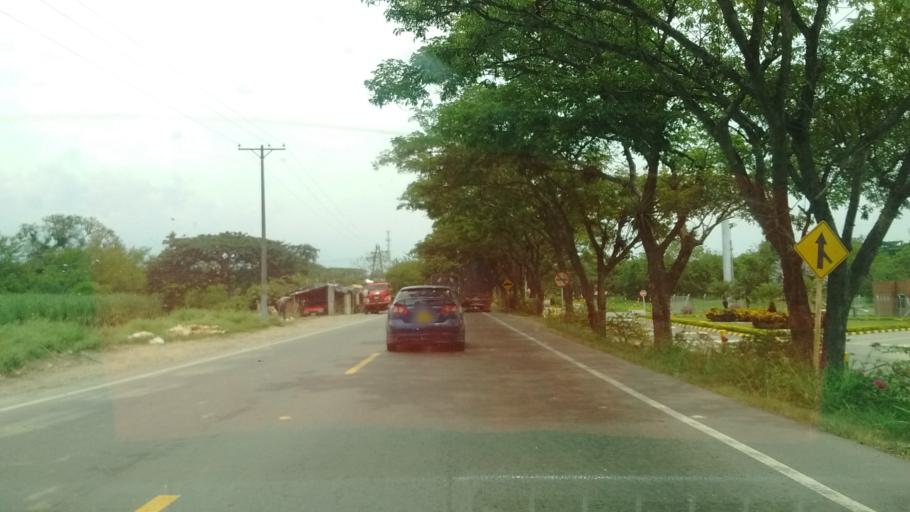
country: CO
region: Valle del Cauca
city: Jamundi
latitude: 3.2985
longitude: -76.4741
